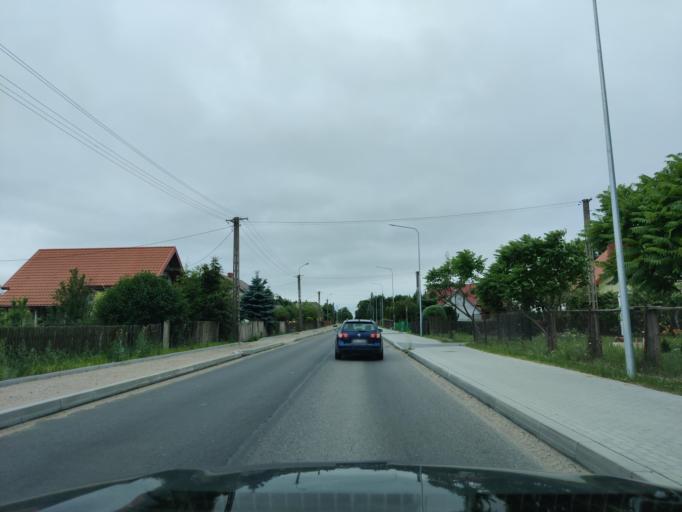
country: PL
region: Warmian-Masurian Voivodeship
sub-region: Powiat szczycienski
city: Rozogi
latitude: 53.4339
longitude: 21.3641
